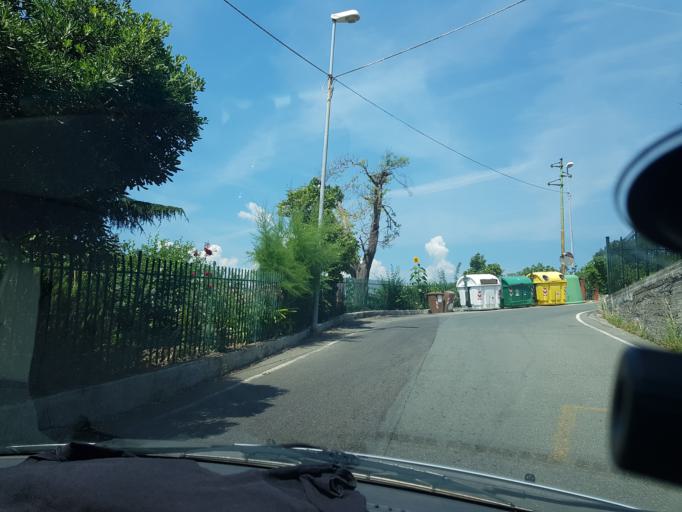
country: IT
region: Liguria
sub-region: Provincia di Genova
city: San Teodoro
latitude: 44.4383
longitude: 8.8382
